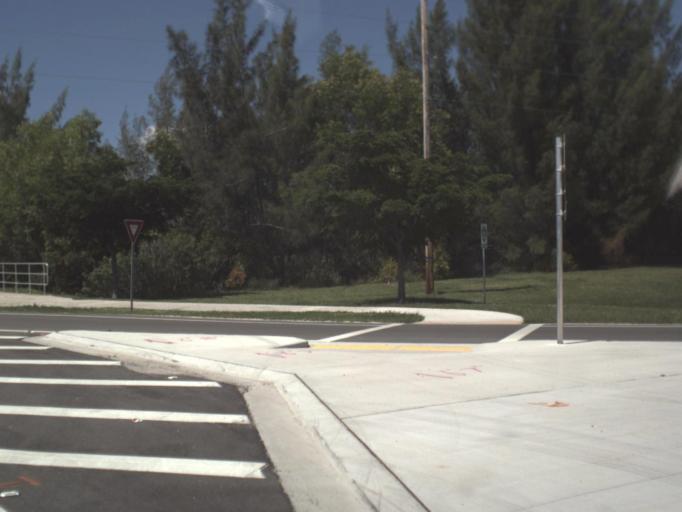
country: US
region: Florida
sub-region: Lee County
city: Cape Coral
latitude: 26.6071
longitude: -82.0152
